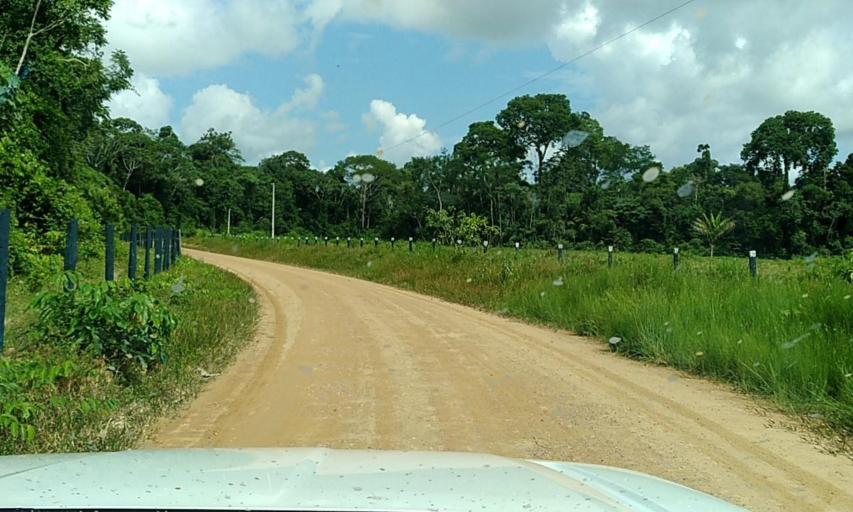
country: BR
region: Para
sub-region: Senador Jose Porfirio
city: Senador Jose Porfirio
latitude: -2.5206
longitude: -51.8366
